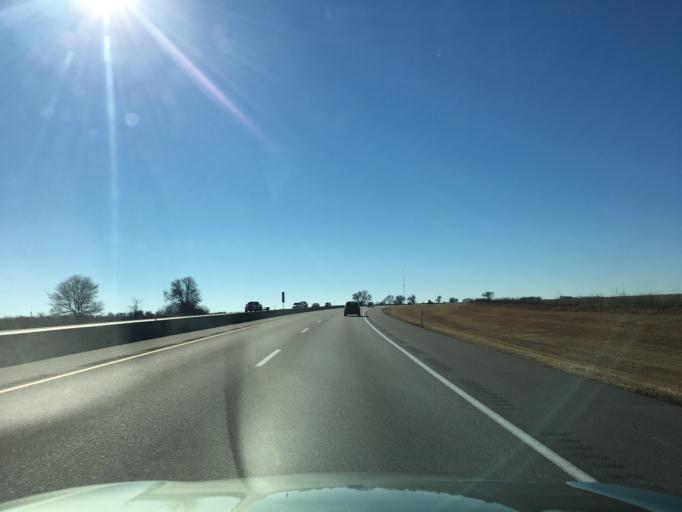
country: US
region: Kansas
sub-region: Sumner County
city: Belle Plaine
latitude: 37.3456
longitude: -97.3223
